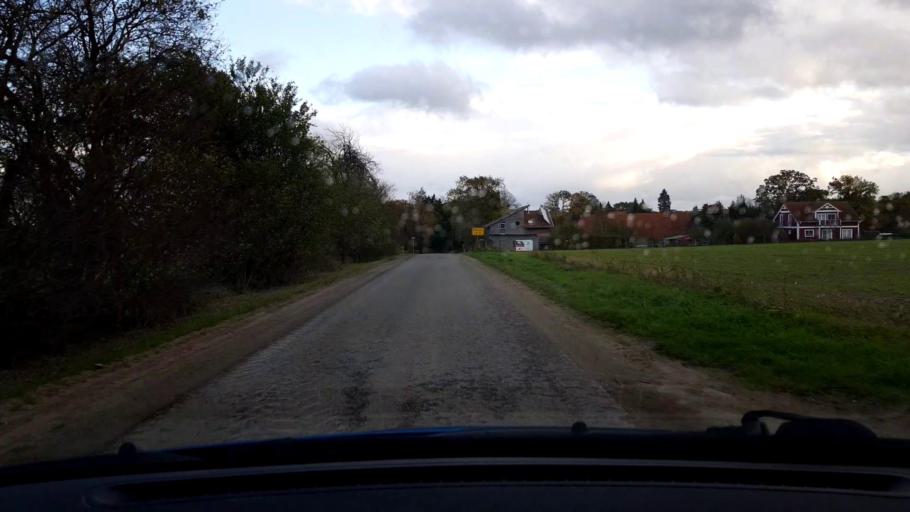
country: DE
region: Lower Saxony
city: Reinstorf
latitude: 53.2441
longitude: 10.5790
